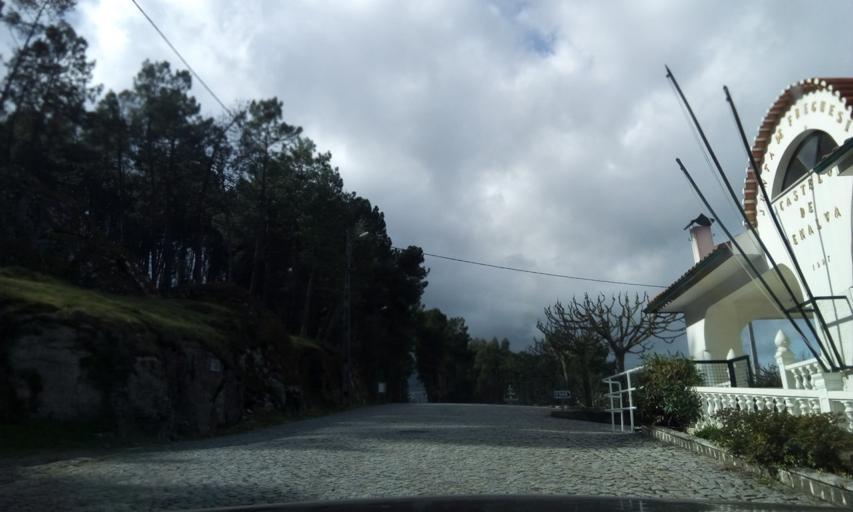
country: PT
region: Viseu
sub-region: Satao
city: Satao
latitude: 40.6607
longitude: -7.6516
